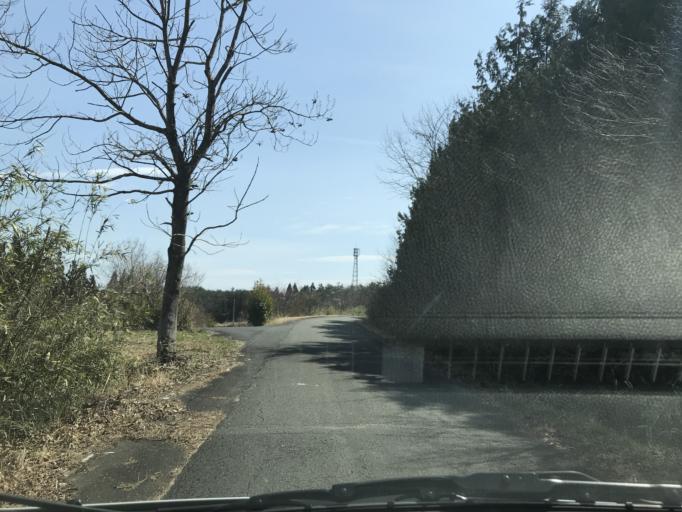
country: JP
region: Iwate
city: Ichinoseki
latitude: 38.8359
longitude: 141.1182
